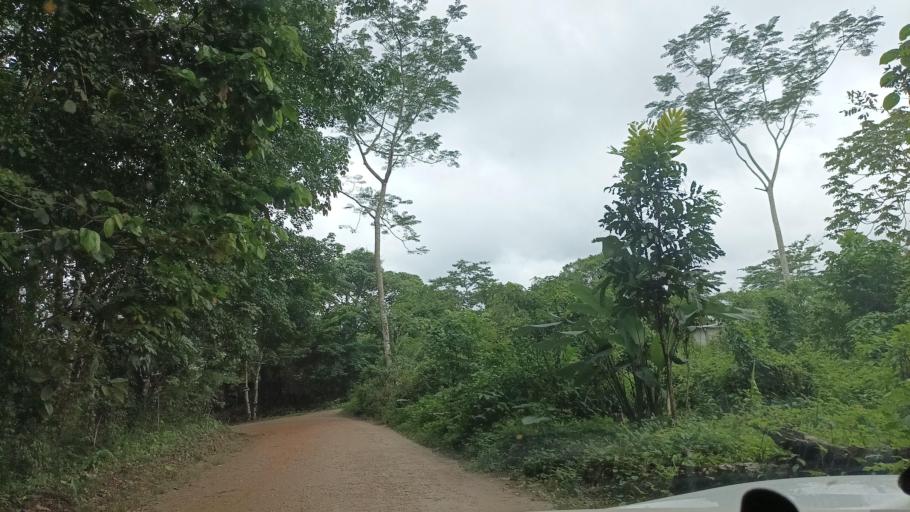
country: MX
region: Veracruz
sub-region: Uxpanapa
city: Poblado 10
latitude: 17.2727
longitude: -94.4959
